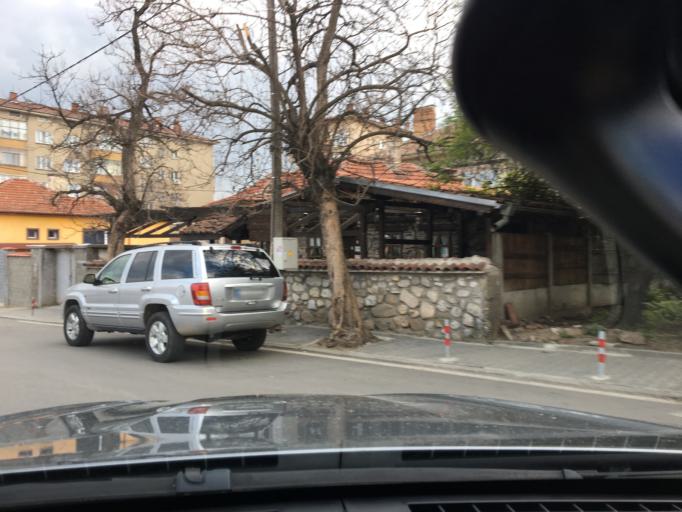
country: BG
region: Stara Zagora
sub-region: Obshtina Kazanluk
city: Kazanluk
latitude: 42.6161
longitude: 25.3895
